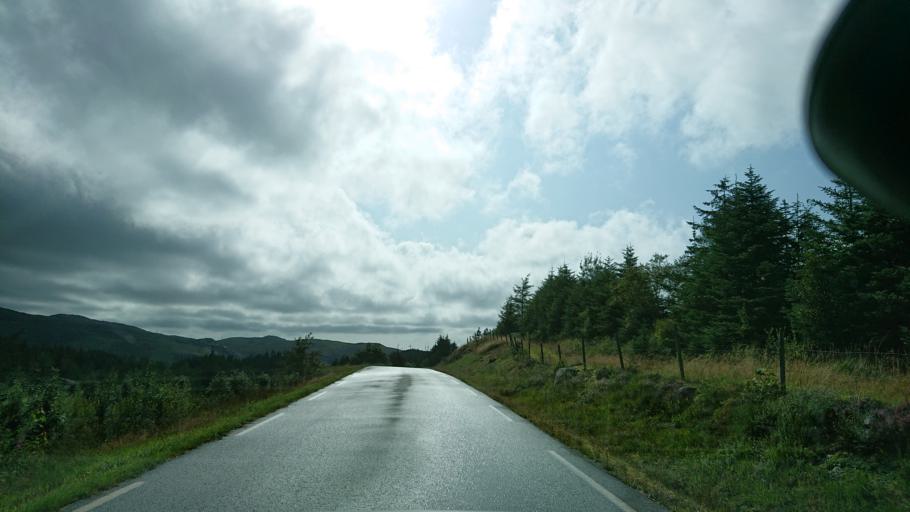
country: NO
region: Rogaland
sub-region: Gjesdal
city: Algard
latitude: 58.6851
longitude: 5.8676
